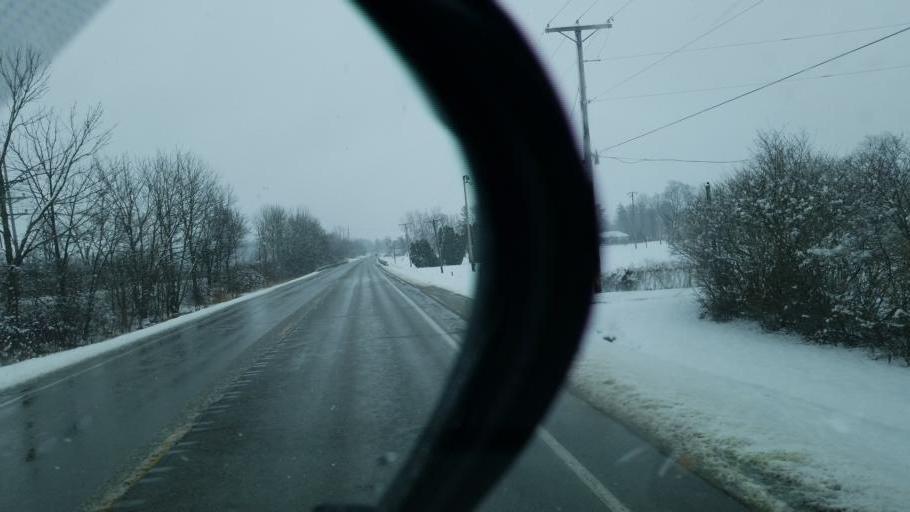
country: US
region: Indiana
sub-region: Delaware County
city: Muncie
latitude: 40.1526
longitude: -85.3455
